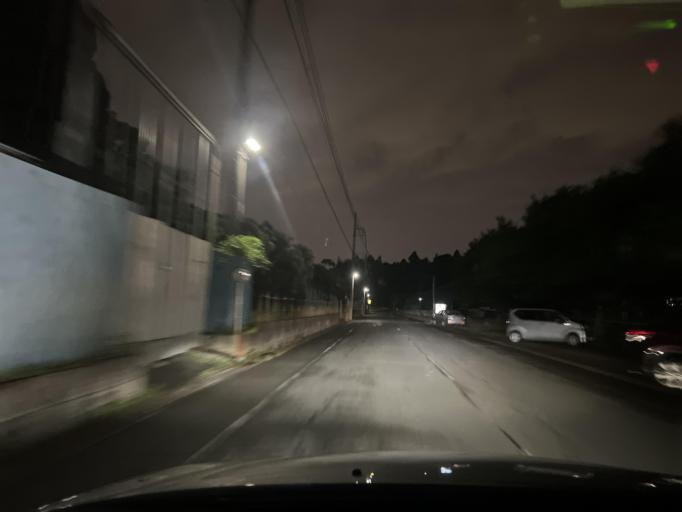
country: JP
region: Chiba
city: Kashiwa
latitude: 35.8391
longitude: 139.9375
